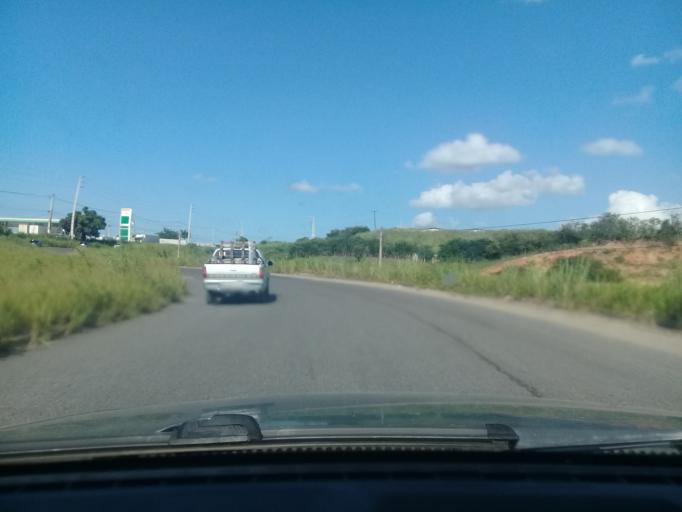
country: BR
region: Pernambuco
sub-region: Vitoria De Santo Antao
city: Vitoria de Santo Antao
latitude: -8.1171
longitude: -35.2660
